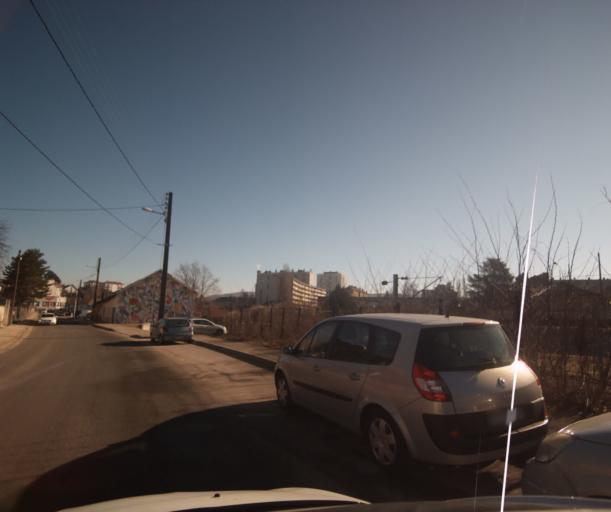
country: FR
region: Franche-Comte
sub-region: Departement du Doubs
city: Besancon
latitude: 47.2430
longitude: 6.0092
